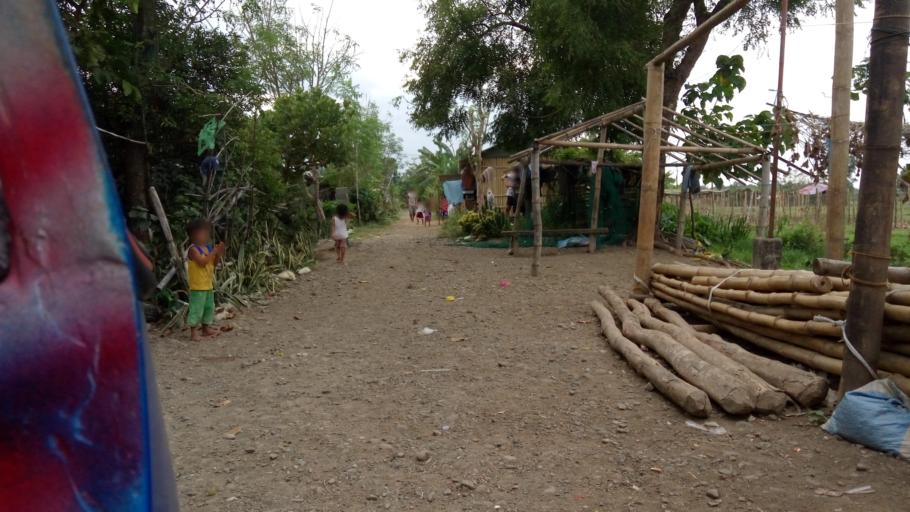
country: PH
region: Ilocos
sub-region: Province of La Union
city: Payocpoc Sur
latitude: 16.4639
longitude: 120.3336
